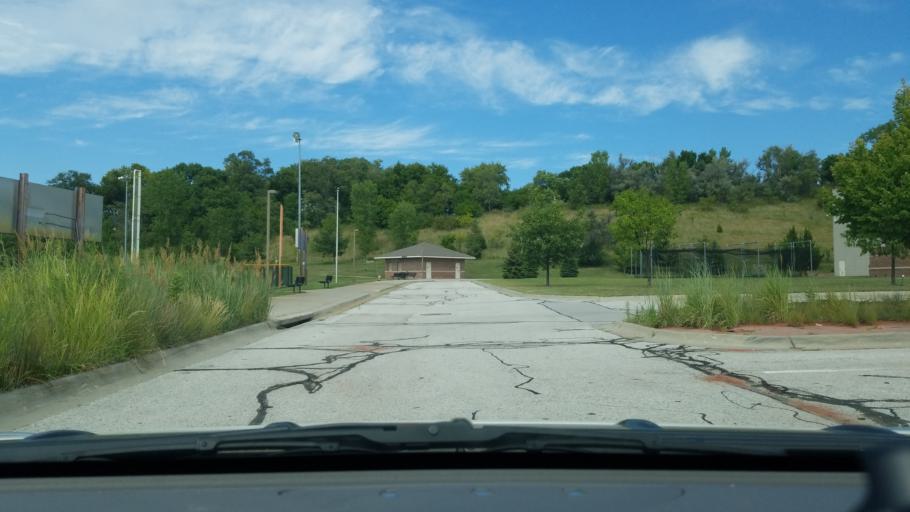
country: US
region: Nebraska
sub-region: Sarpy County
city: Offutt Air Force Base
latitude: 41.1421
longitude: -95.9305
